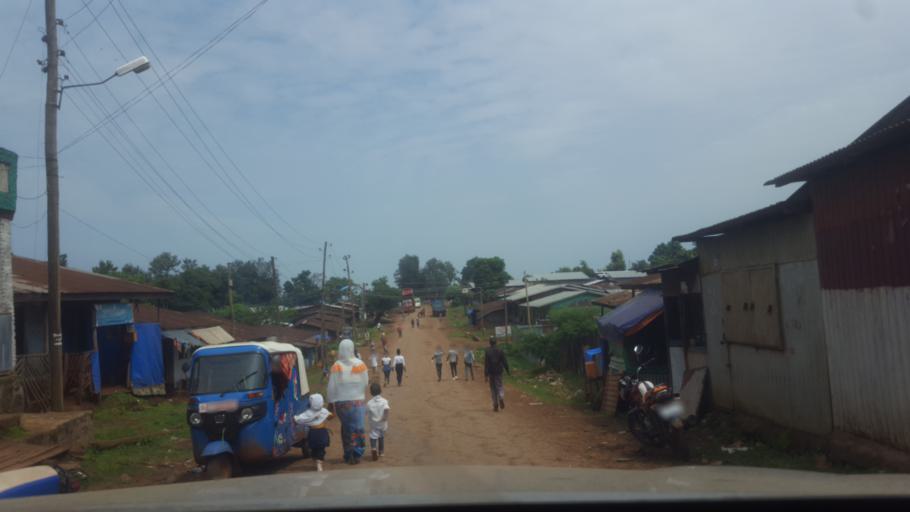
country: ET
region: Southern Nations, Nationalities, and People's Region
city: Tippi
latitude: 7.2347
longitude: 35.3184
